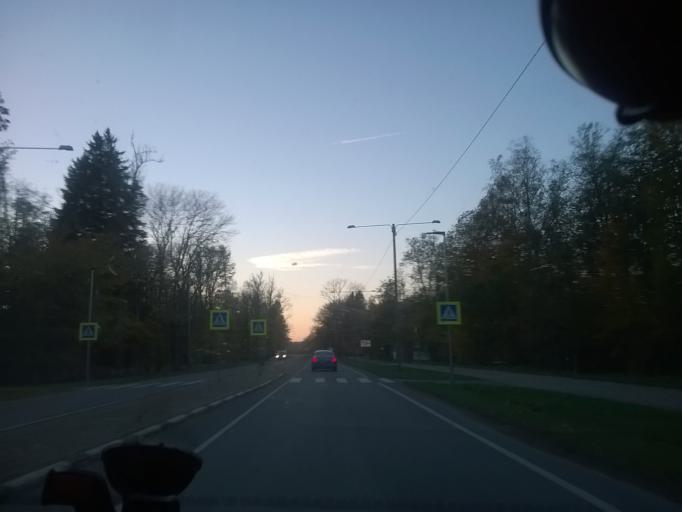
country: EE
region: Laeaene
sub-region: Ridala Parish
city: Uuemoisa
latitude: 58.9563
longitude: 23.7490
